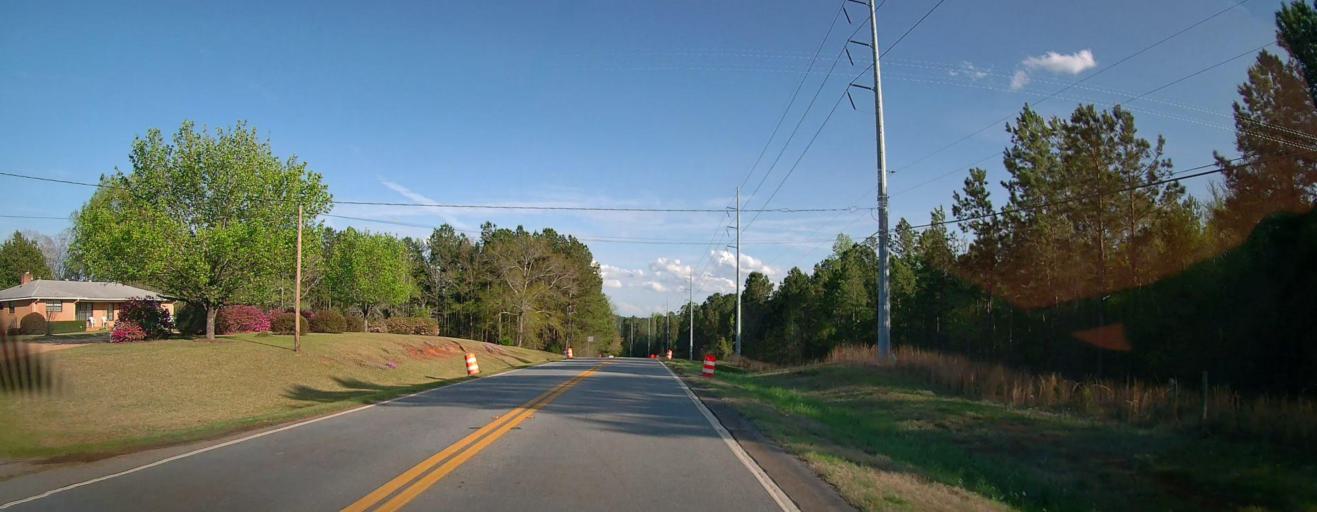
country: US
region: Georgia
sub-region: Baldwin County
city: Milledgeville
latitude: 33.1046
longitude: -83.2766
